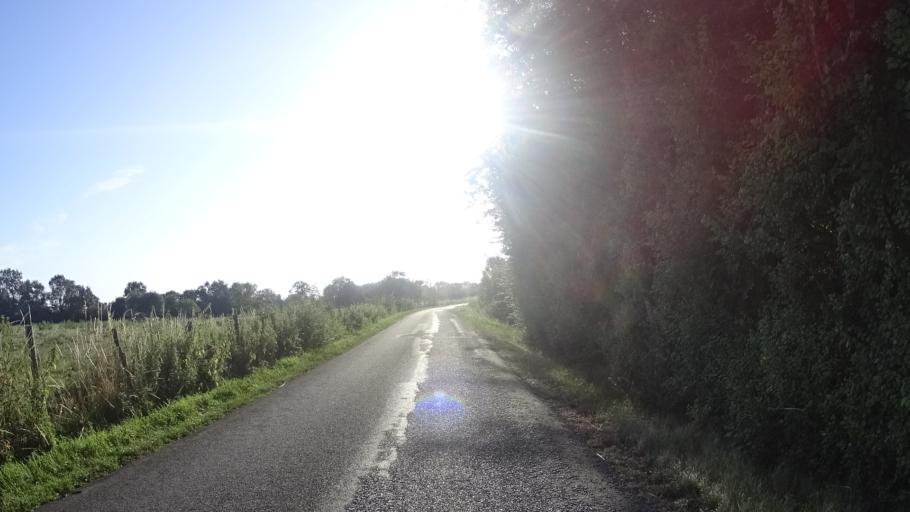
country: FR
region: Pays de la Loire
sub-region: Departement de Maine-et-Loire
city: Villebernier
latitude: 47.2724
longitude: -0.0204
